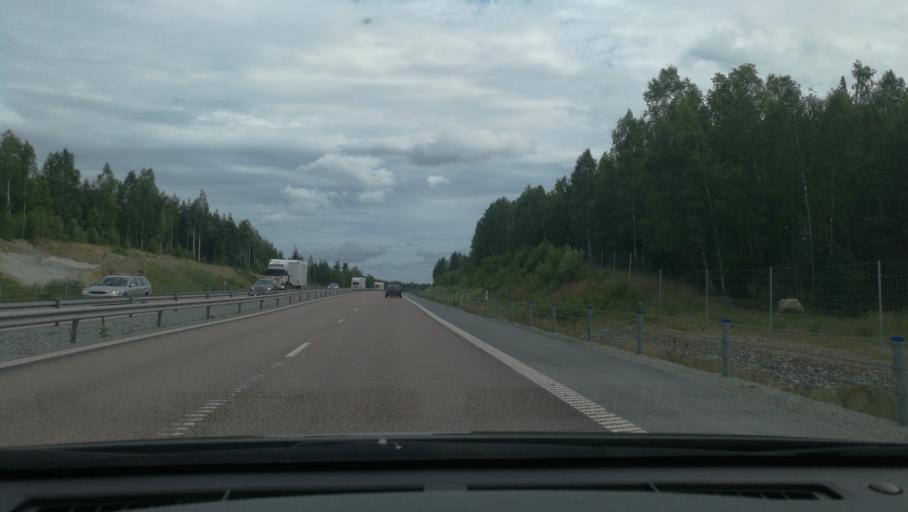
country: SE
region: Vaestmanland
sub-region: Vasteras
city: Tillberga
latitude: 59.6241
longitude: 16.7082
